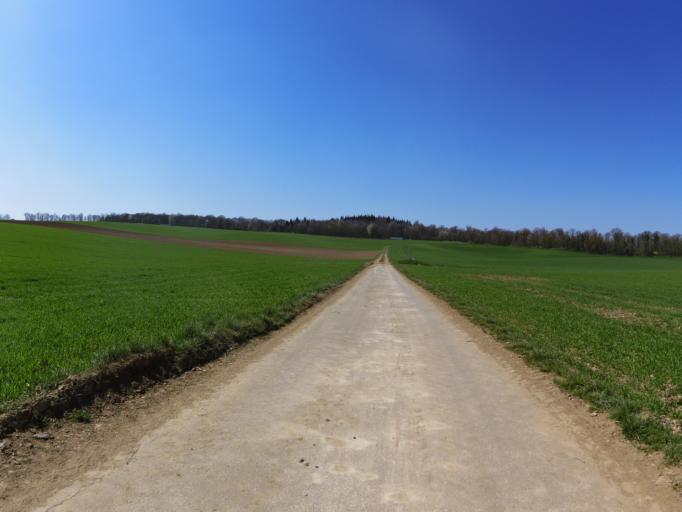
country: DE
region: Bavaria
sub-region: Regierungsbezirk Unterfranken
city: Rottendorf
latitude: 49.8138
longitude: 10.0504
